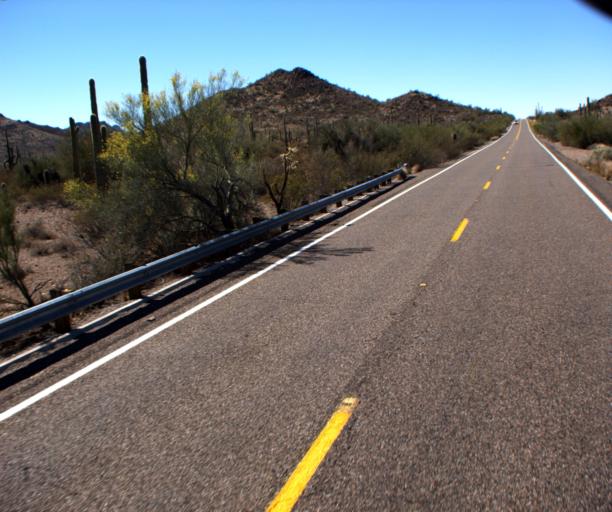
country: MX
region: Sonora
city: Sonoyta
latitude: 32.0898
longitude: -112.7754
